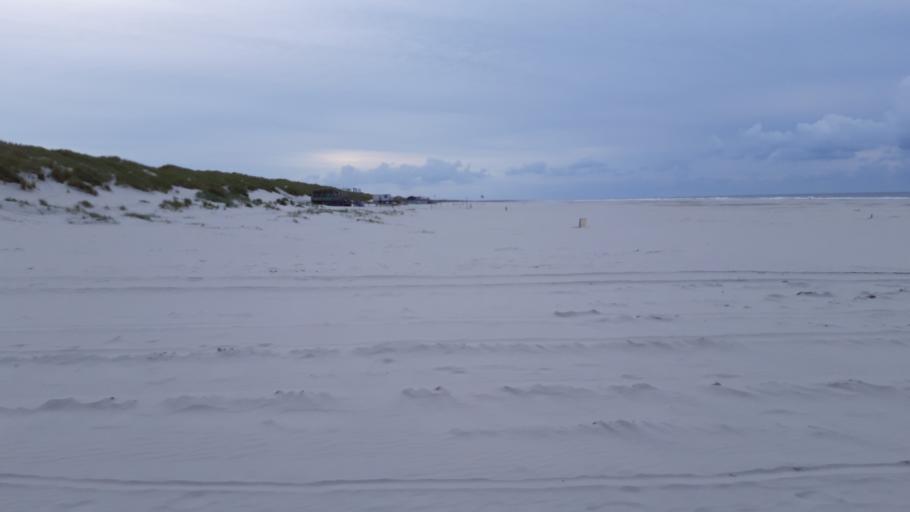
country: NL
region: Friesland
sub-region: Gemeente Ameland
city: Nes
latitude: 53.4594
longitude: 5.7582
